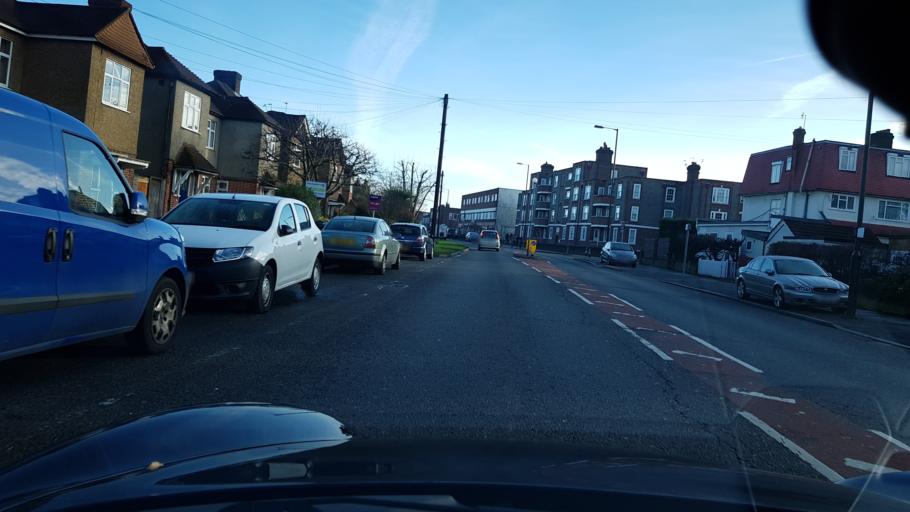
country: GB
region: England
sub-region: Greater London
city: Morden
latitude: 51.4033
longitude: -0.2118
